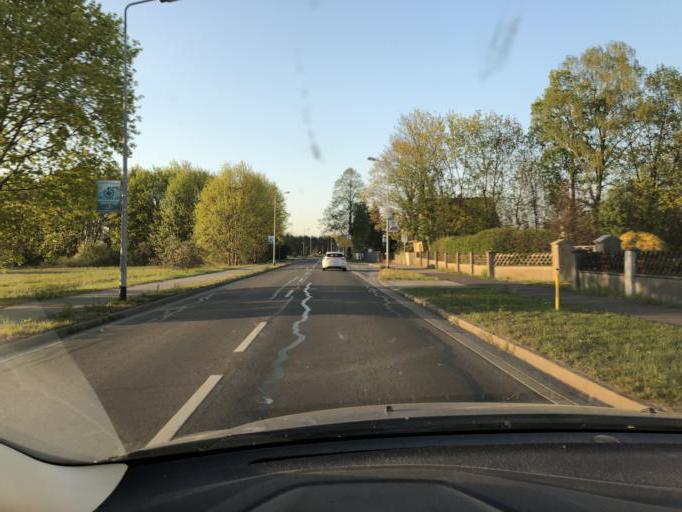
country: DE
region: Brandenburg
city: Spremberg
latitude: 51.5463
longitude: 14.3444
